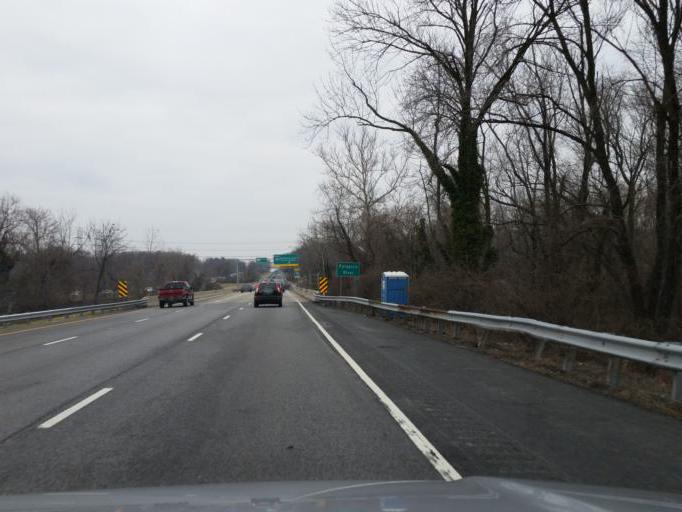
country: US
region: Maryland
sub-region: Baltimore County
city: Baltimore Highlands
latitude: 39.2283
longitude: -76.6502
